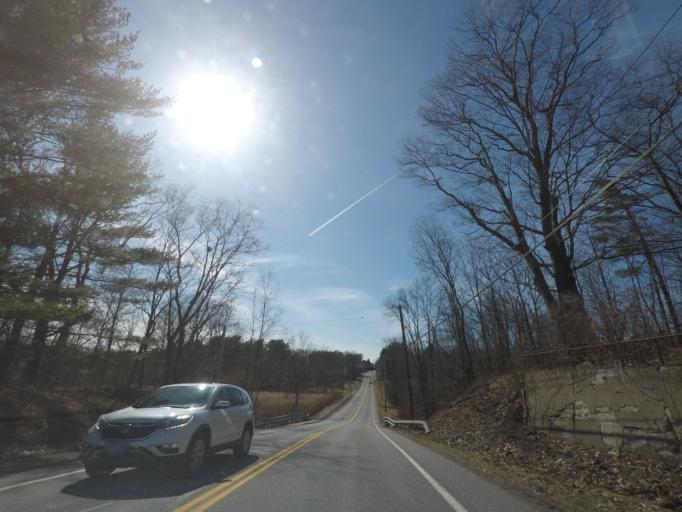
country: US
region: New York
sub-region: Saratoga County
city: Ballston Spa
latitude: 43.0020
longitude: -73.8326
